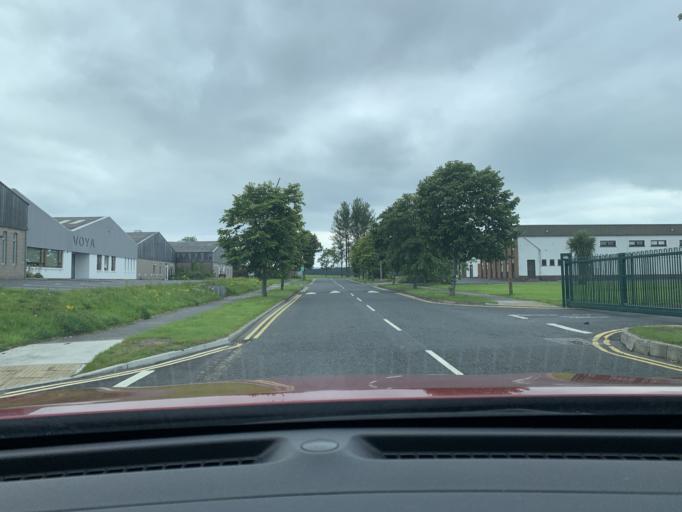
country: IE
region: Connaught
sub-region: Sligo
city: Sligo
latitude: 54.2749
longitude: -8.4956
